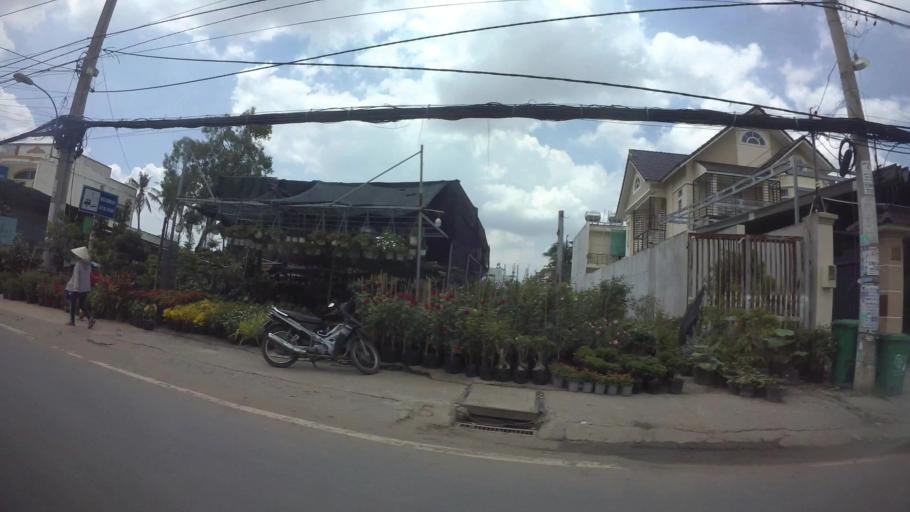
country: VN
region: Ho Chi Minh City
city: Quan Chin
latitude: 10.8340
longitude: 106.7830
